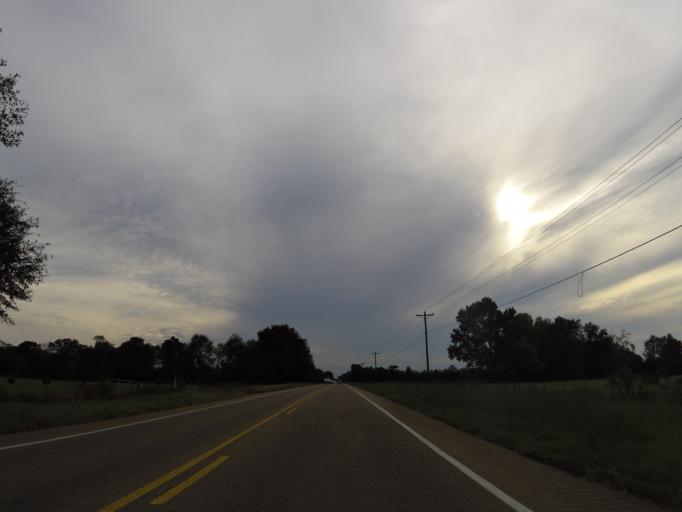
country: US
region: Alabama
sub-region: Monroe County
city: Frisco City
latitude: 31.4503
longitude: -87.3768
